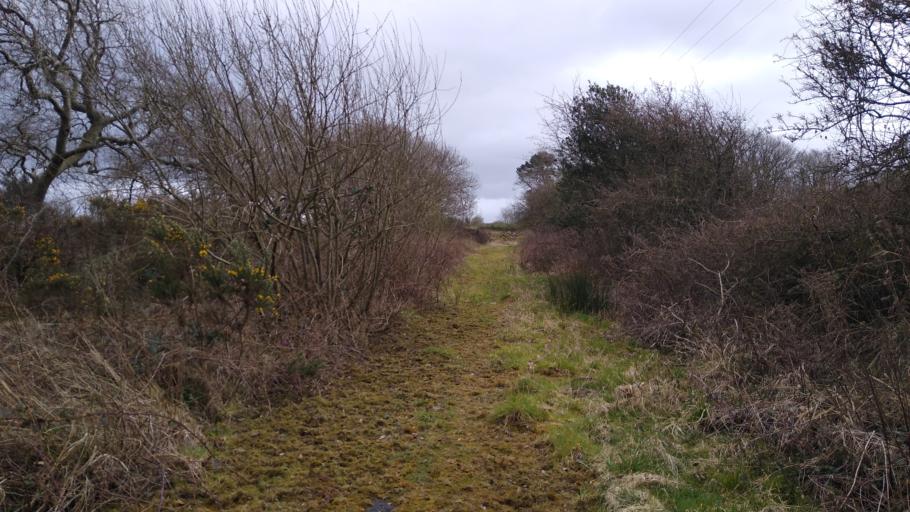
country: GB
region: England
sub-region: Cumbria
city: Dearham
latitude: 54.6919
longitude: -3.4405
